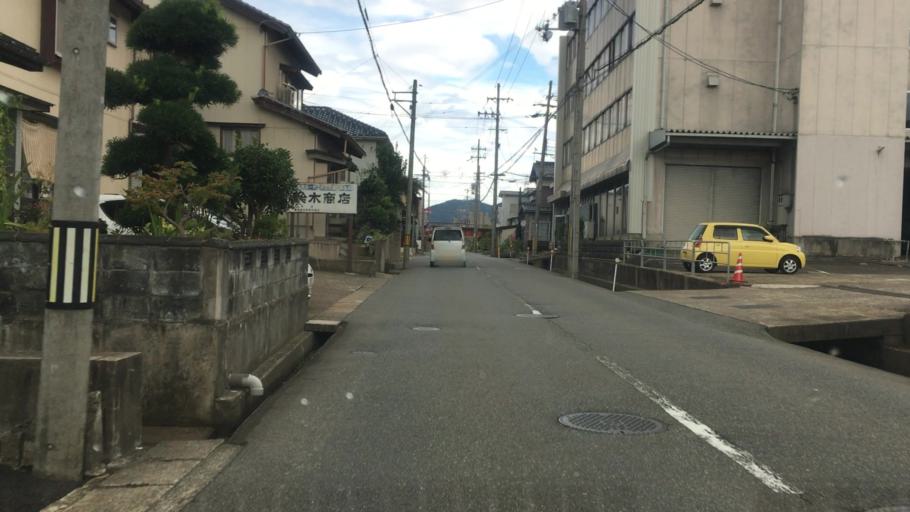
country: JP
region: Hyogo
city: Toyooka
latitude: 35.5495
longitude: 134.8130
